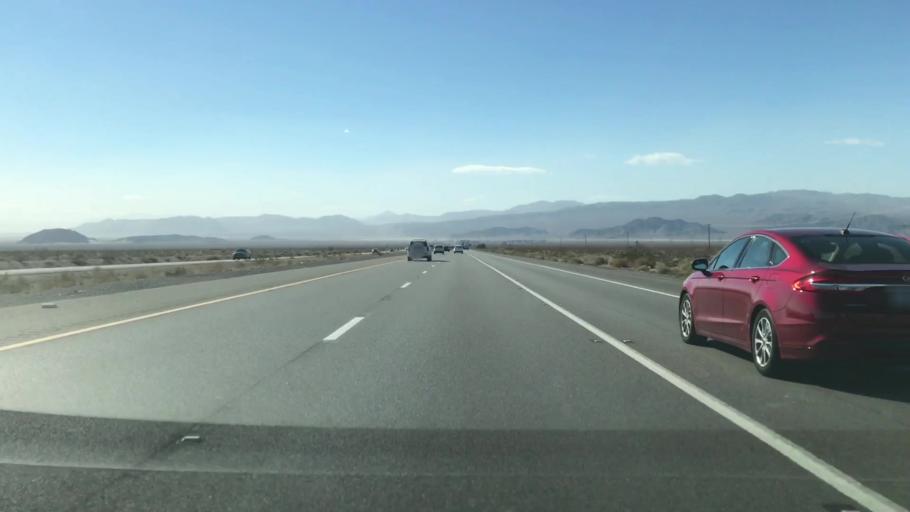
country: US
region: Nevada
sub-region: Clark County
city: Sandy Valley
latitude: 35.3197
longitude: -115.9896
